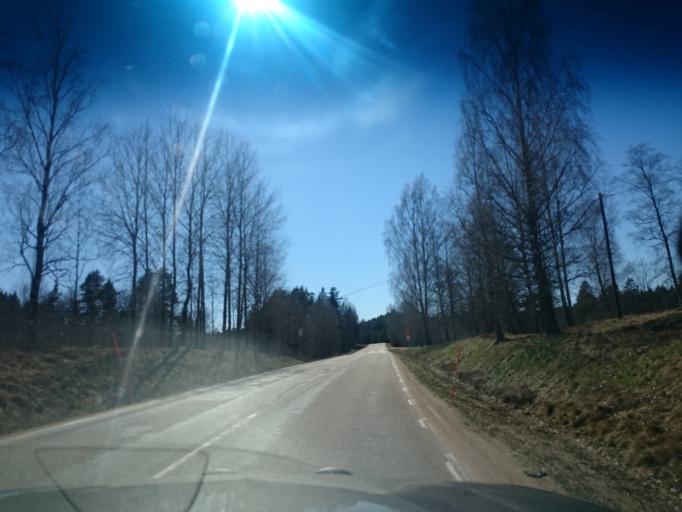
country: SE
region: Joenkoeping
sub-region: Vetlanda Kommun
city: Landsbro
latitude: 57.2183
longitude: 14.9522
